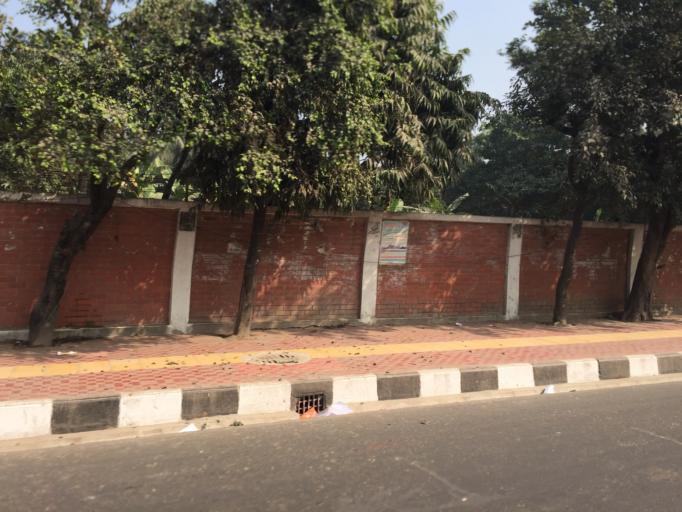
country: BD
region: Dhaka
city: Azimpur
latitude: 23.7672
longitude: 90.3697
